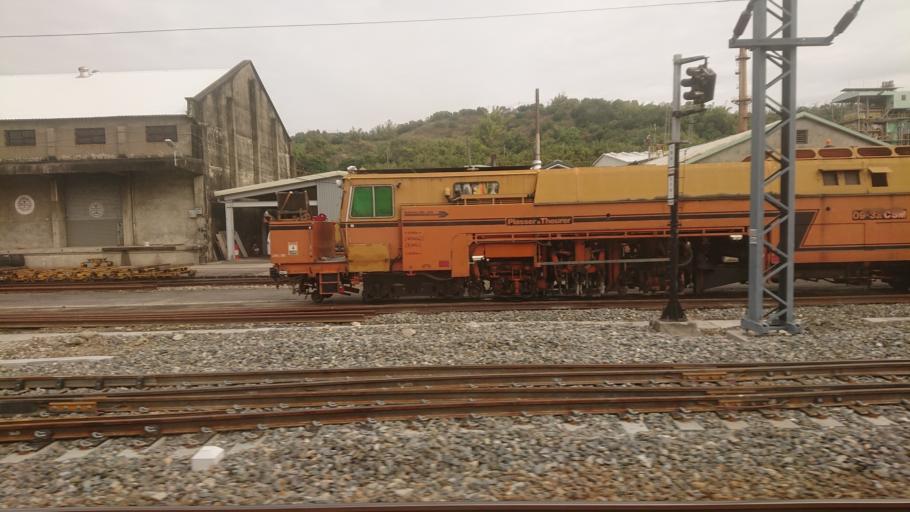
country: TW
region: Taiwan
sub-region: Changhua
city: Chang-hua
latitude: 24.1151
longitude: 120.5888
